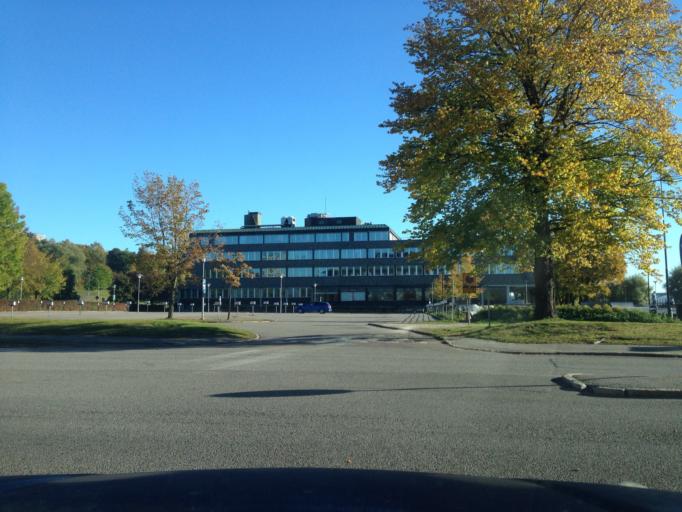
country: SE
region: Vaesternorrland
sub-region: Sundsvalls Kommun
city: Sundsvall
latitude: 62.3933
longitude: 17.3089
